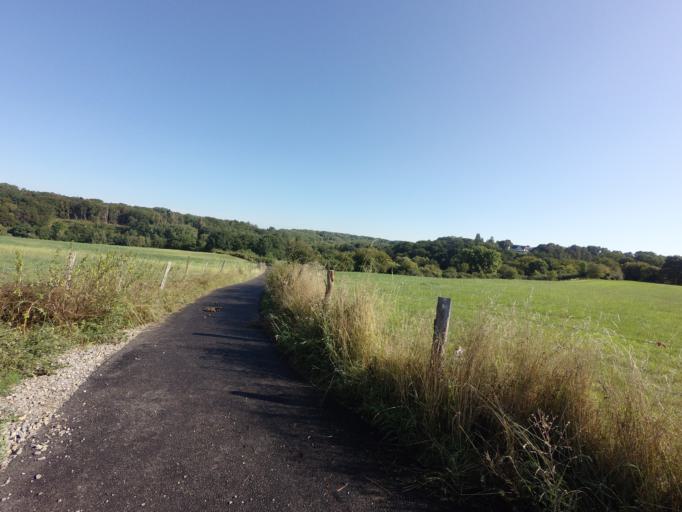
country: DE
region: North Rhine-Westphalia
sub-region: Regierungsbezirk Koln
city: Wurselen
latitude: 50.8204
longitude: 6.1081
